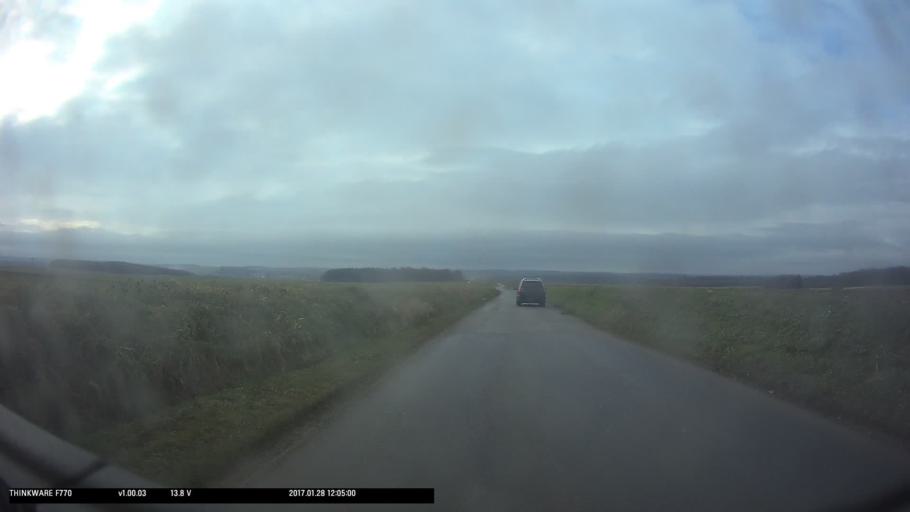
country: FR
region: Ile-de-France
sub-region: Departement du Val-d'Oise
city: Marines
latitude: 49.1208
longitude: 1.9915
